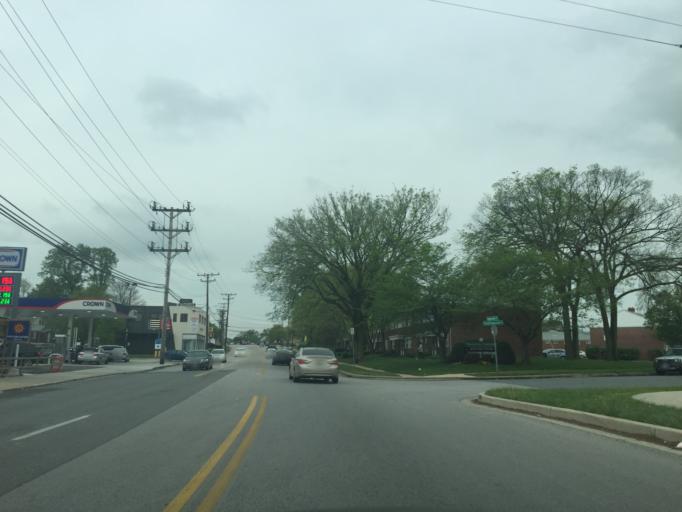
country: US
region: Maryland
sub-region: Baltimore County
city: Catonsville
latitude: 39.2924
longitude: -76.7316
